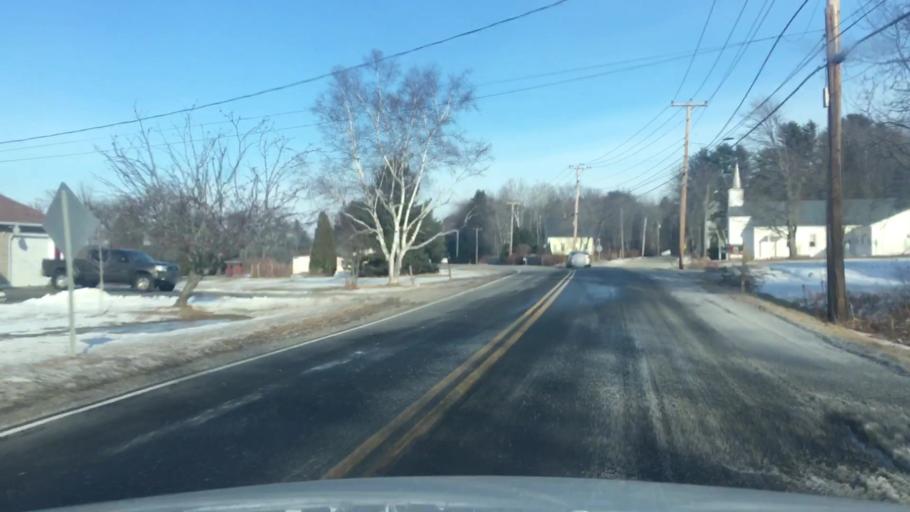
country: US
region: Maine
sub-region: Androscoggin County
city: Minot
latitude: 44.0517
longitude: -70.2759
